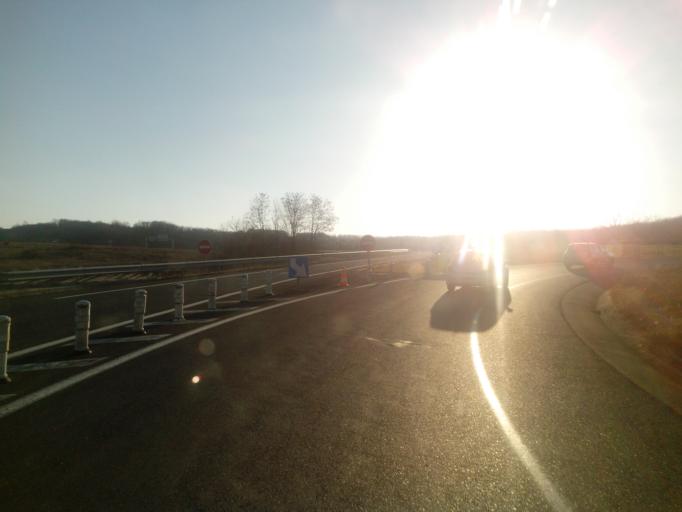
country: FR
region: Limousin
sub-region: Departement de la Correze
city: Brive-la-Gaillarde
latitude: 45.0628
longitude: 1.5079
